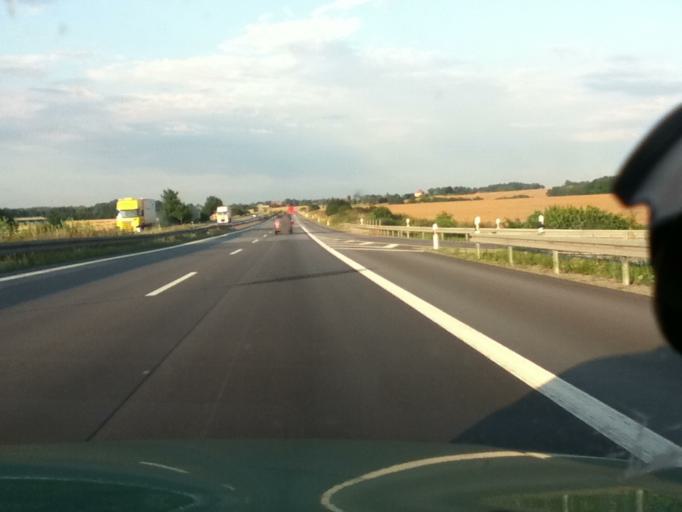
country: DE
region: Saxony
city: Panschwitz-Kuckau
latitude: 51.1983
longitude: 14.2238
